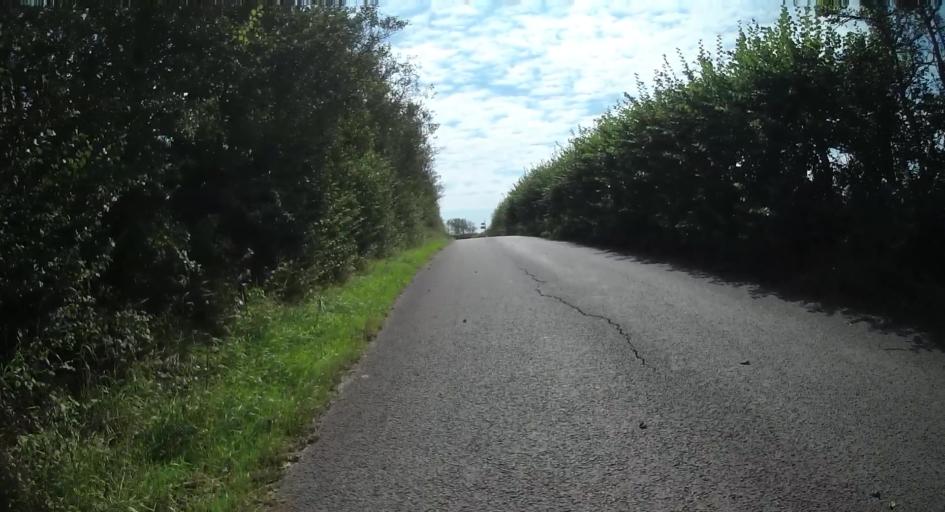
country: GB
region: England
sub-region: Isle of Wight
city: Chale
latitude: 50.6382
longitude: -1.3752
